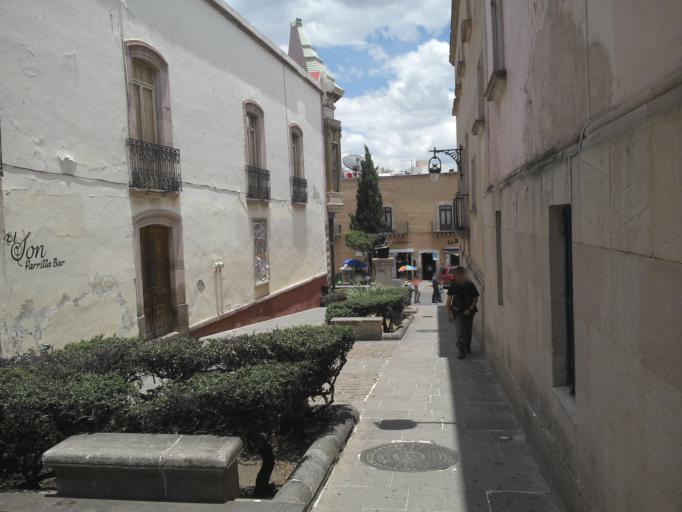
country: MX
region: Zacatecas
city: Zacatecas
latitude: 22.7750
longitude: -102.5736
